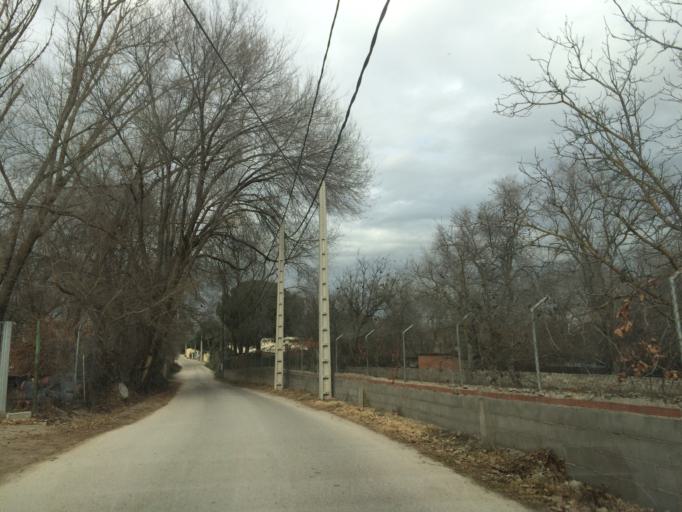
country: ES
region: Madrid
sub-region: Provincia de Madrid
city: Arroyomolinos
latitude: 40.3098
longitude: -3.9464
